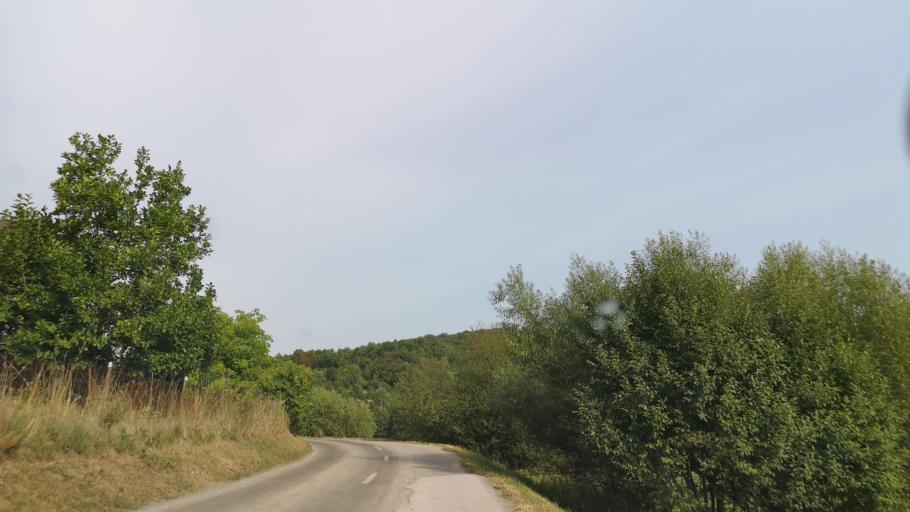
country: SK
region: Banskobystricky
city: Revuca
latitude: 48.6022
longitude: 20.0900
